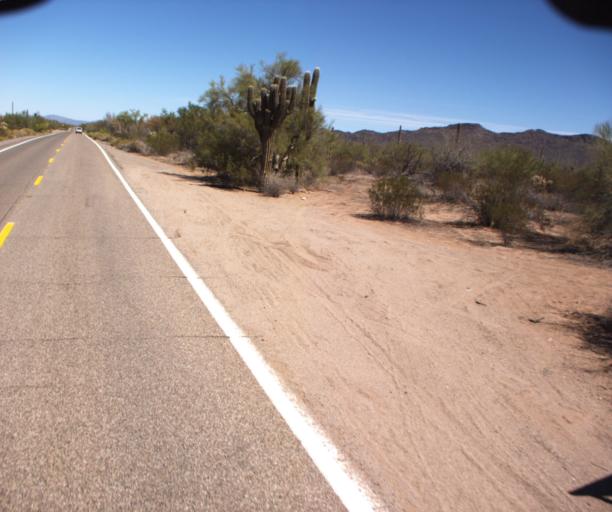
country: US
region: Arizona
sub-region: Pima County
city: Ajo
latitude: 32.1738
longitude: -112.7625
